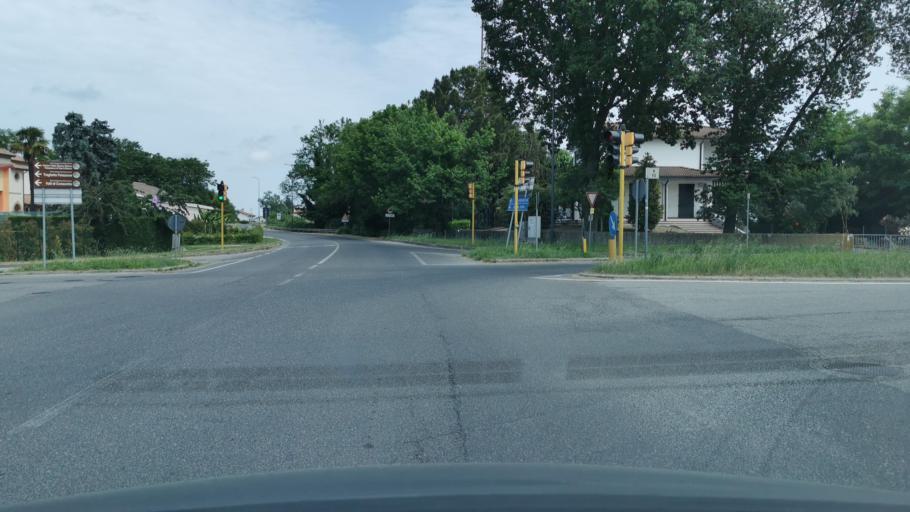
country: IT
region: Emilia-Romagna
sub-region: Provincia di Ravenna
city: Sant'Alberto
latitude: 44.5371
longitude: 12.1611
